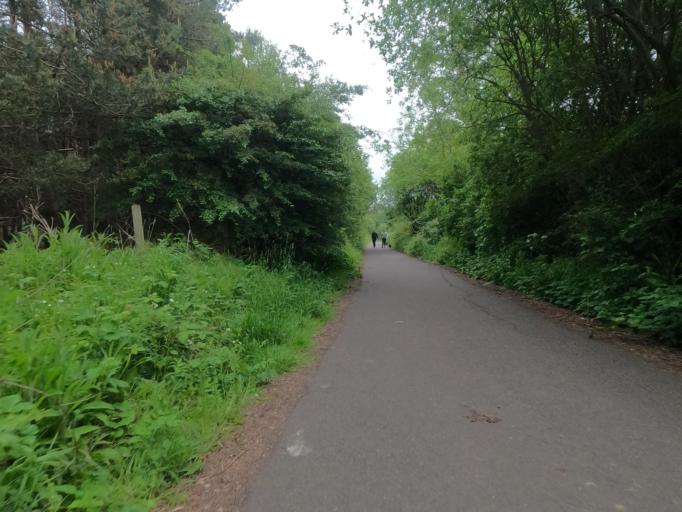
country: GB
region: England
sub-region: Northumberland
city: Bedlington
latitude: 55.1226
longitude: -1.5642
